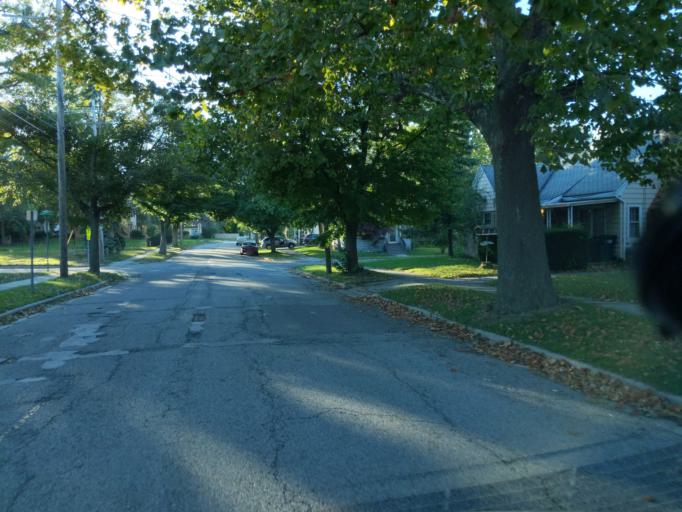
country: US
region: Michigan
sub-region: Ingham County
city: Lansing
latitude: 42.7327
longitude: -84.5711
